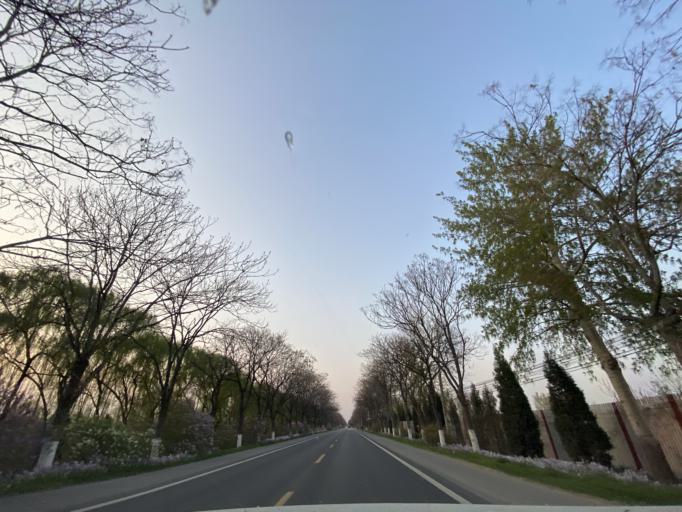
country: CN
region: Beijing
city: Weishanzhuang
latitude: 39.6073
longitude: 116.4096
